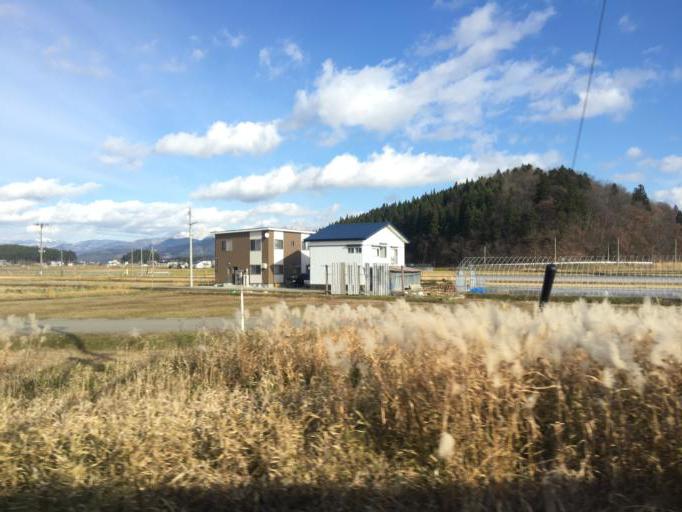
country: JP
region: Akita
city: Yokotemachi
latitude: 39.3668
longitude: 140.5373
